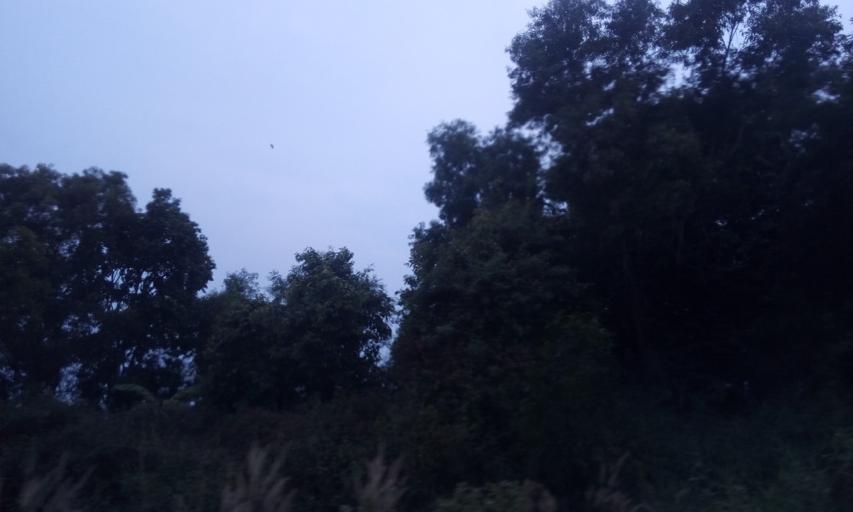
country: TH
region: Chachoengsao
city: Plaeng Yao
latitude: 13.5922
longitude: 101.1993
